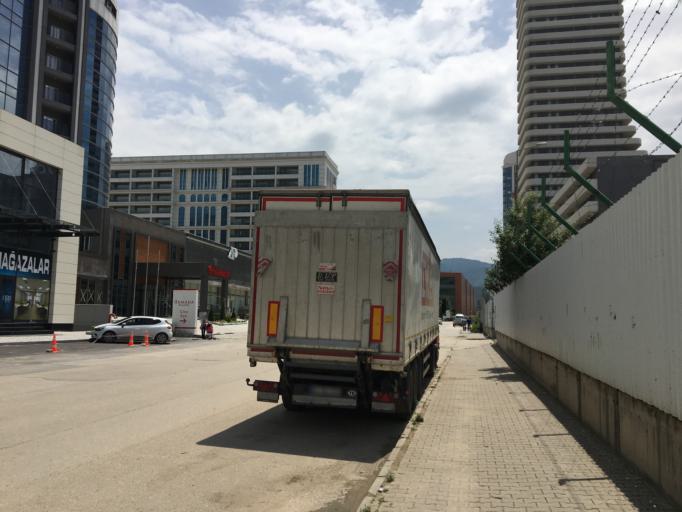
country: TR
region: Bursa
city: Yildirim
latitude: 40.2100
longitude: 28.9974
